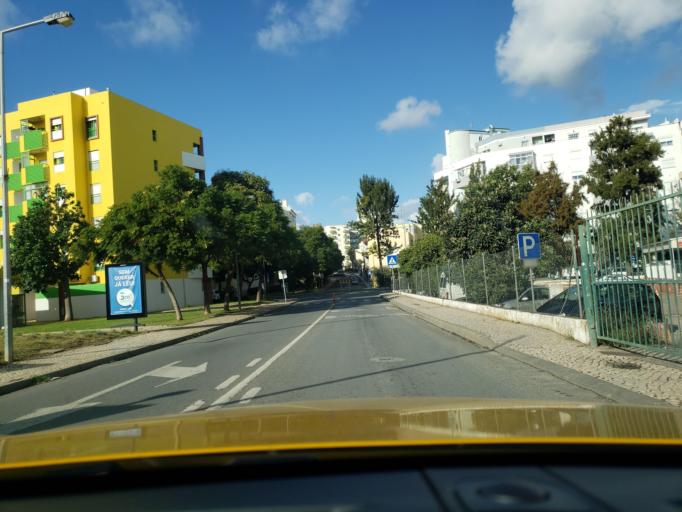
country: PT
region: Faro
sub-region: Portimao
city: Portimao
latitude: 37.1453
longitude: -8.5406
